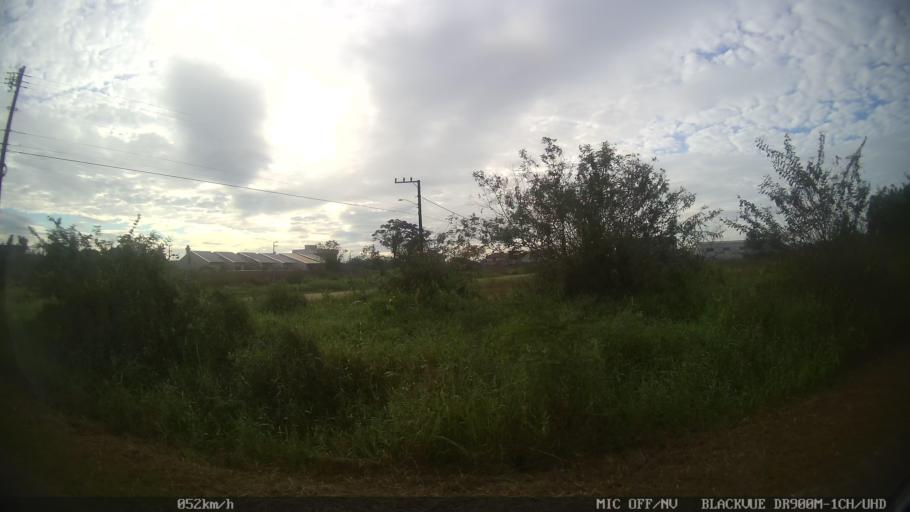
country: BR
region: Santa Catarina
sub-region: Barra Velha
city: Barra Velha
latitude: -26.6269
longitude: -48.7014
